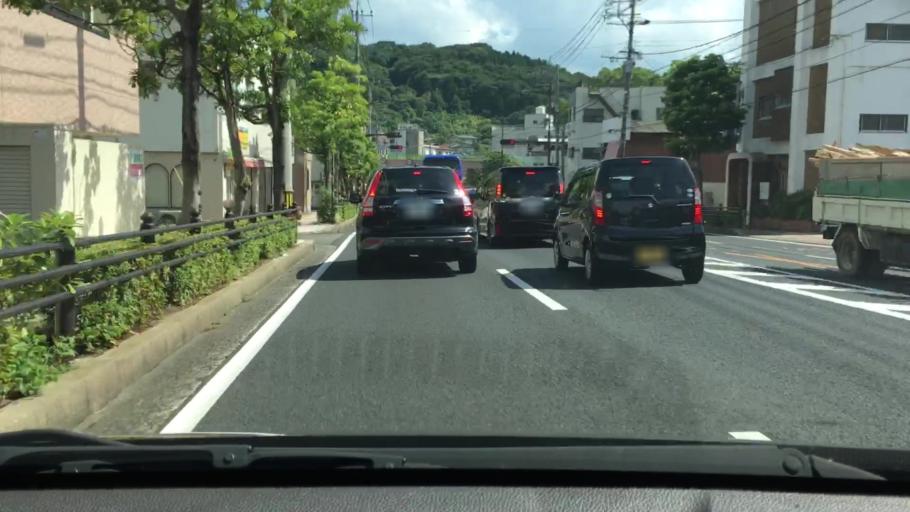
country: JP
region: Nagasaki
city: Sasebo
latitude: 33.1990
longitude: 129.7221
